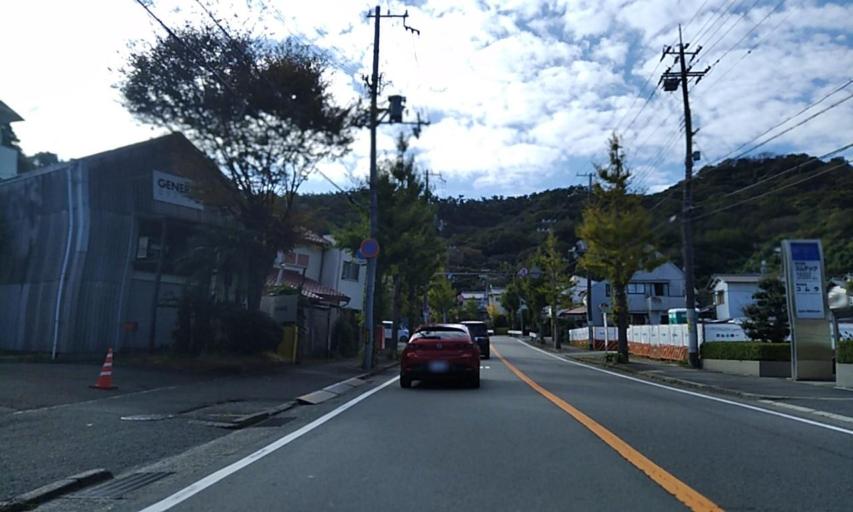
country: JP
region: Wakayama
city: Minato
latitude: 34.1931
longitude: 135.1591
